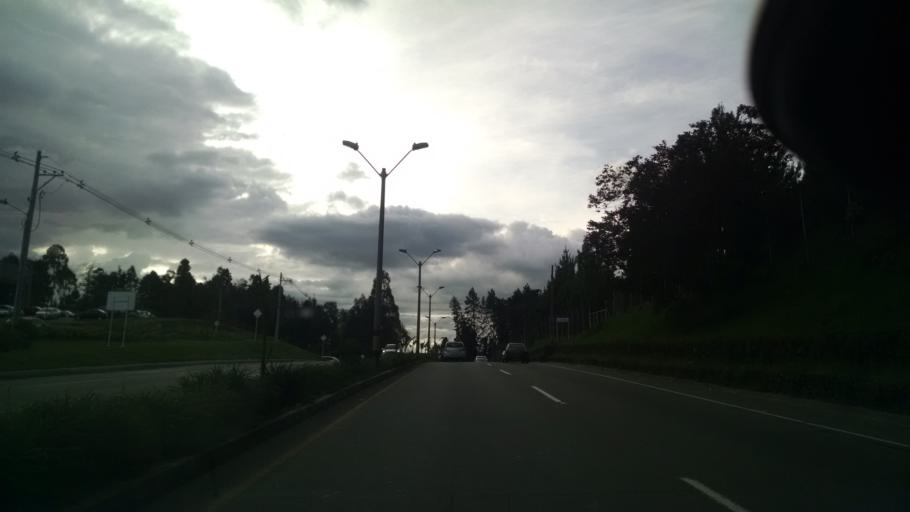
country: CO
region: Antioquia
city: Envigado
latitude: 6.1535
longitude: -75.5410
